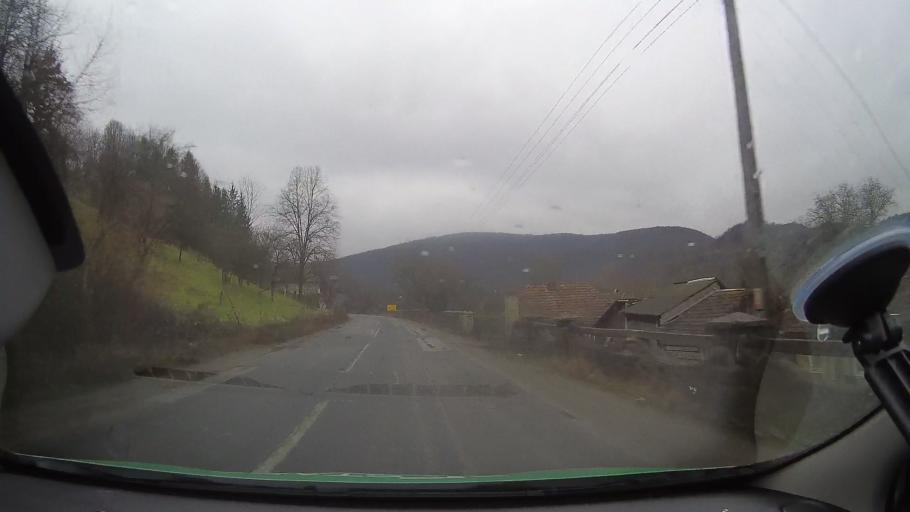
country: RO
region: Arad
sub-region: Comuna Halmagiu
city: Halmagiu
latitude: 46.2400
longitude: 22.5606
